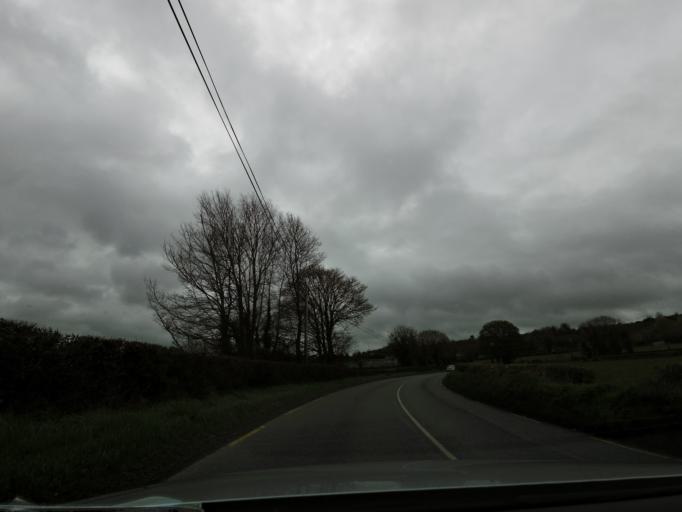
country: IE
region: Leinster
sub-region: Kilkenny
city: Kilkenny
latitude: 52.7051
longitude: -7.3113
